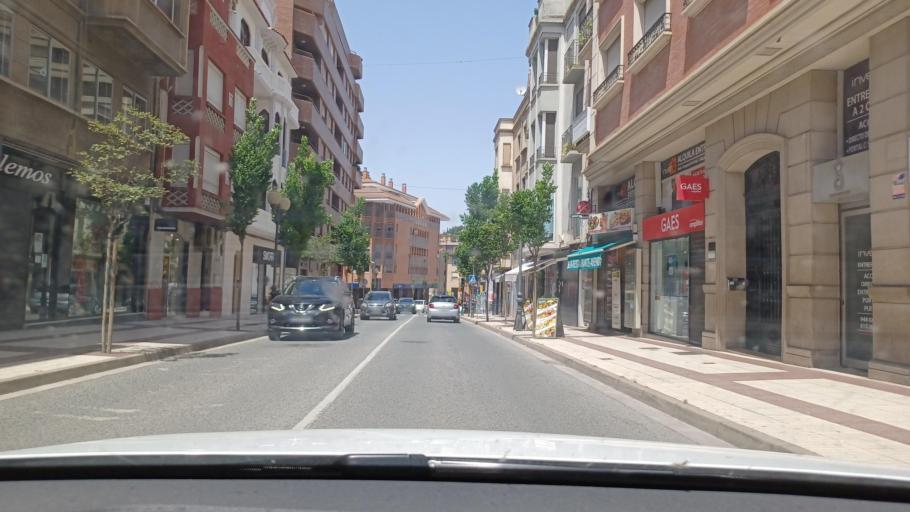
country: ES
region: Navarre
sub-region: Provincia de Navarra
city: Tudela
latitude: 42.0615
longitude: -1.6026
